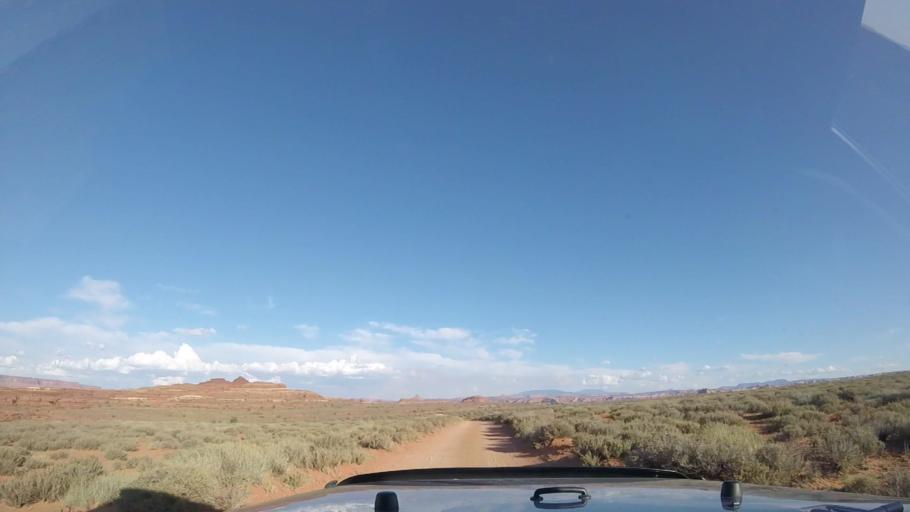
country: US
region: Utah
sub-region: Grand County
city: Moab
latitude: 38.2139
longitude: -109.7916
